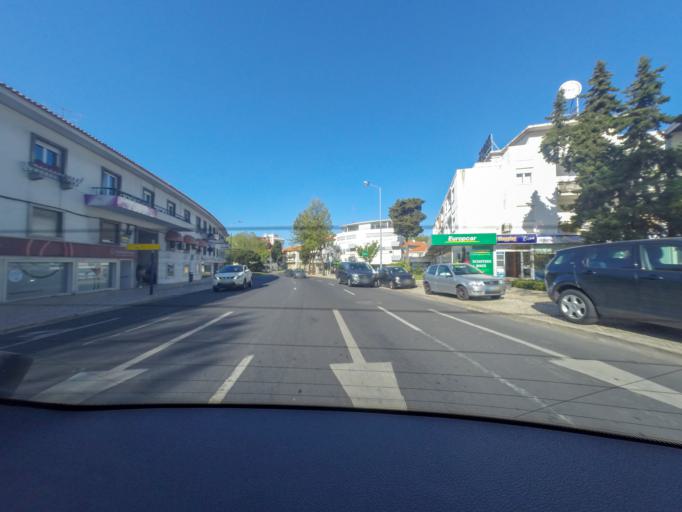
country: PT
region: Lisbon
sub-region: Cascais
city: Monte Estoril
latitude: 38.7010
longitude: -9.4192
